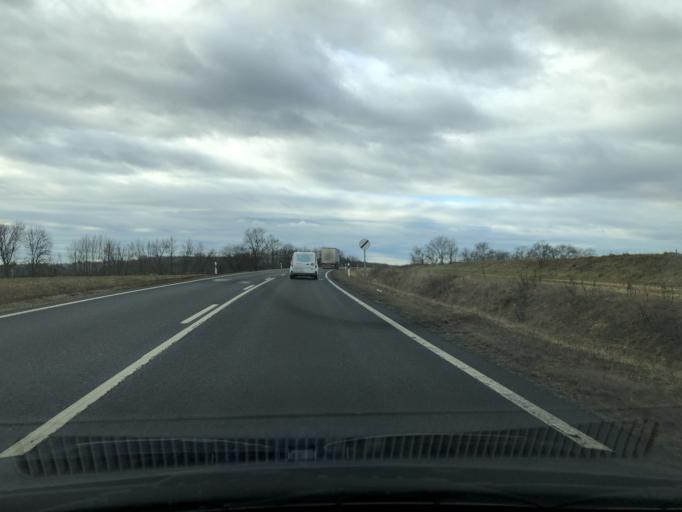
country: HU
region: Vas
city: Gencsapati
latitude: 47.2533
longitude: 16.5808
